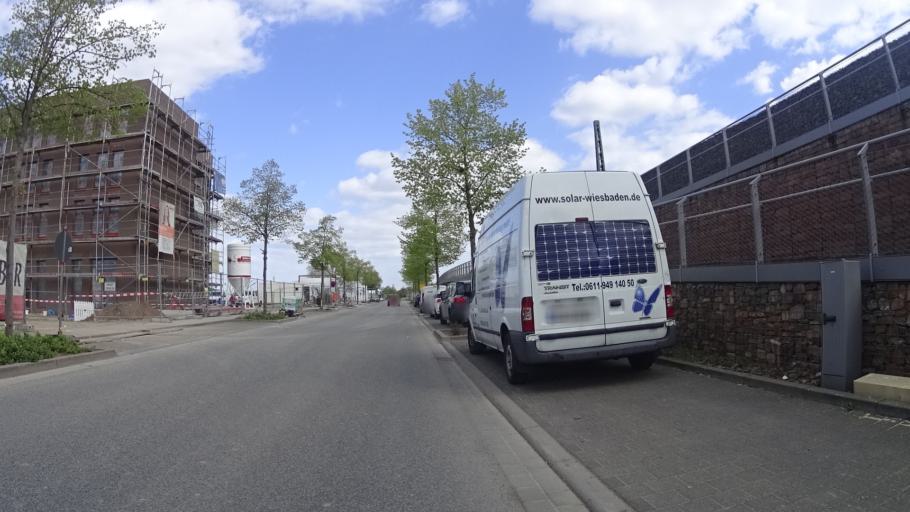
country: DE
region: Rheinland-Pfalz
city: Bingen am Rhein
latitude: 49.9701
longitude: 7.9112
